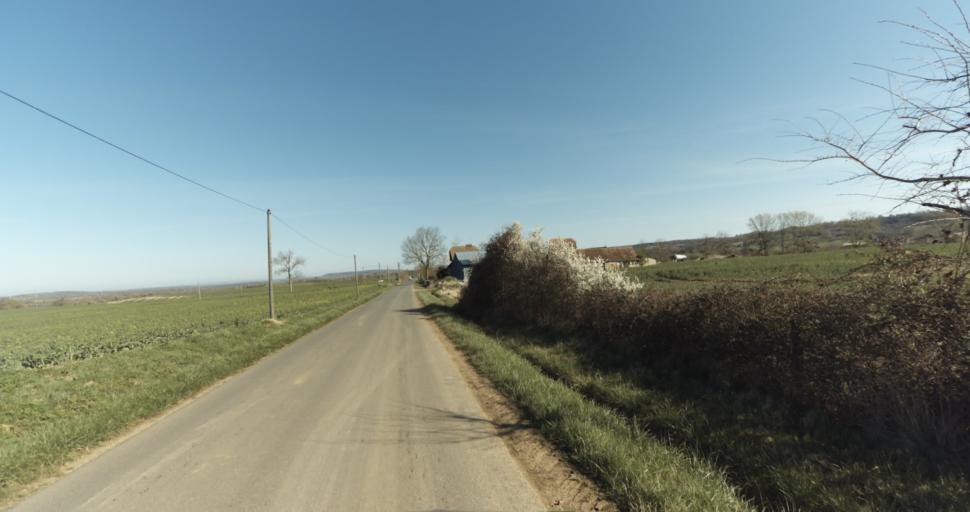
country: FR
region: Lower Normandy
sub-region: Departement de l'Orne
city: Trun
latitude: 48.9017
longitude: 0.0326
